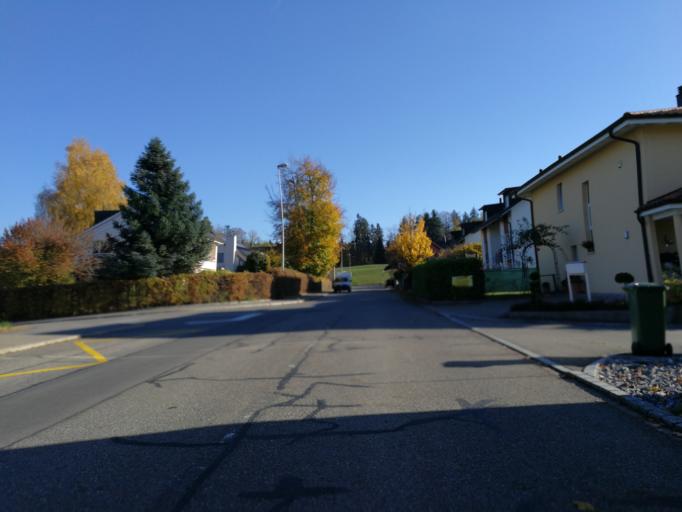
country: CH
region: Zurich
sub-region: Bezirk Meilen
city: Oetwil am See
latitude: 47.2654
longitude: 8.7253
